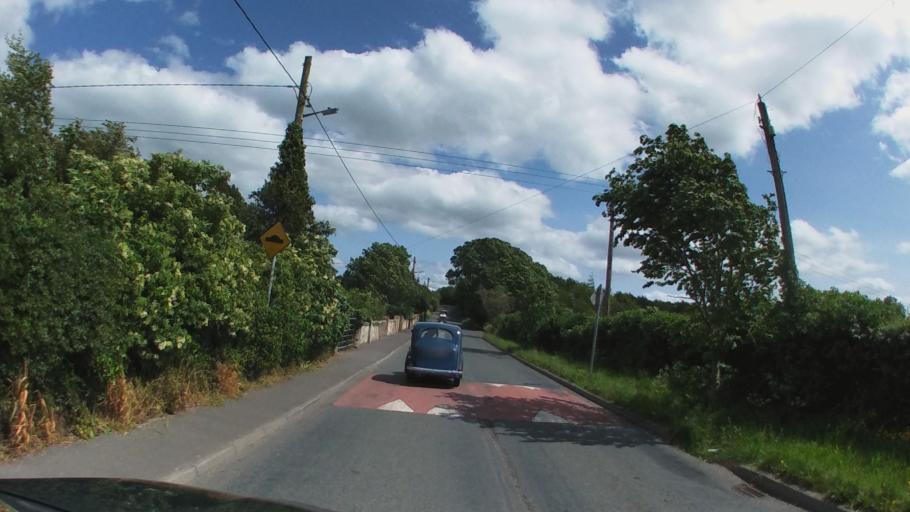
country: IE
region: Leinster
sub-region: Kildare
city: Moone
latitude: 53.0086
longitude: -6.8100
